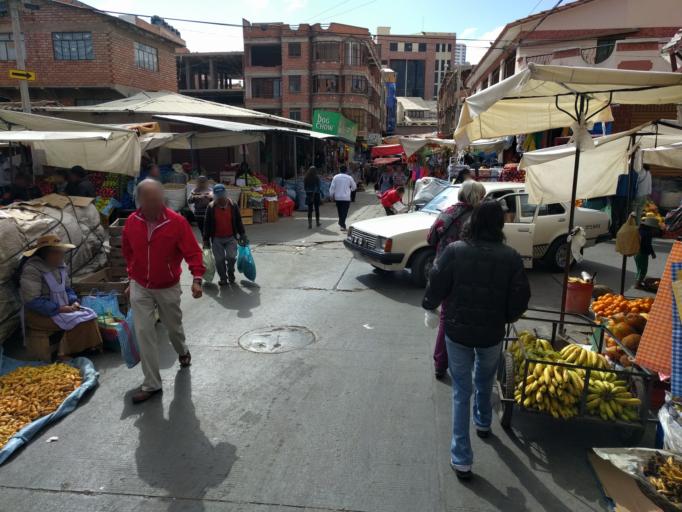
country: BO
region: Chuquisaca
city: Sucre
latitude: -19.0362
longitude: -65.2534
